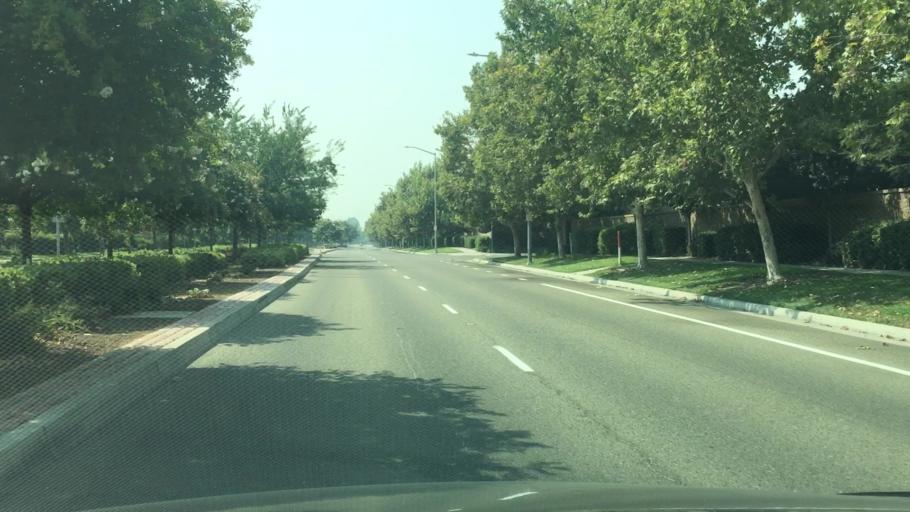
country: US
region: California
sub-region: Fresno County
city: Clovis
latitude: 36.8656
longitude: -119.7022
